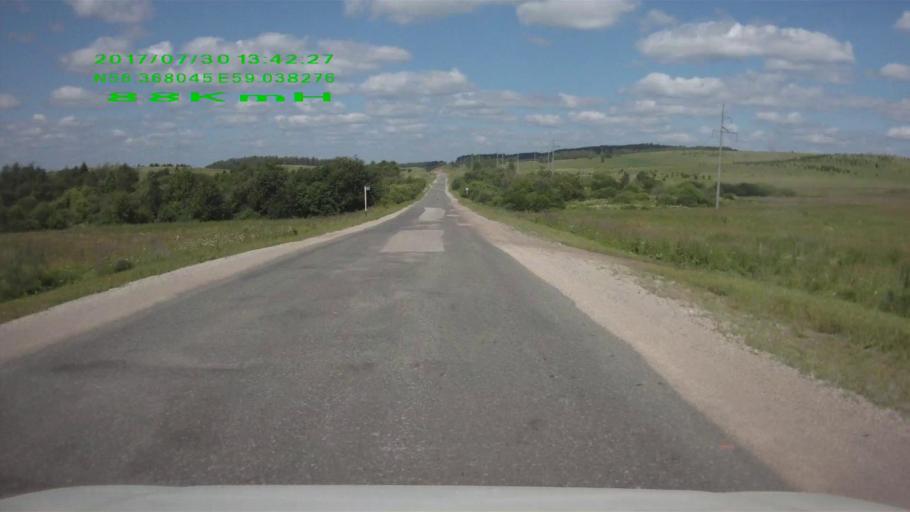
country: RU
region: Sverdlovsk
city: Mikhaylovsk
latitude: 56.3686
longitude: 59.0383
